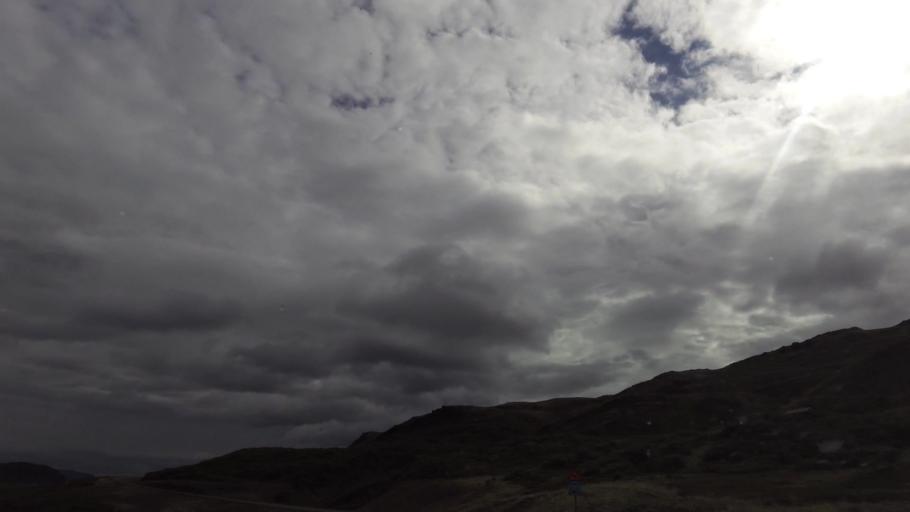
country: IS
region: West
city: Stykkisholmur
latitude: 65.5235
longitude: -22.1215
